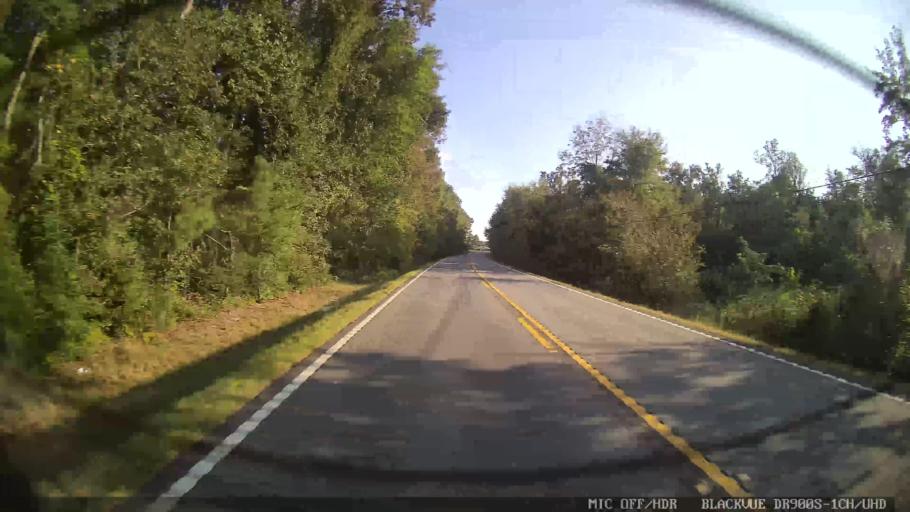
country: US
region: Tennessee
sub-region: Bradley County
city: Wildwood Lake
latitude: 34.9658
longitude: -84.7733
